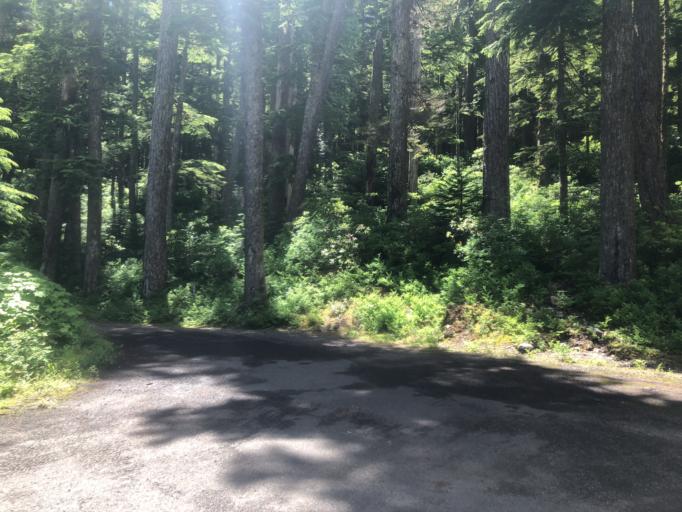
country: US
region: Oregon
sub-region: Clackamas County
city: Mount Hood Village
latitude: 45.4616
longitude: -121.8518
